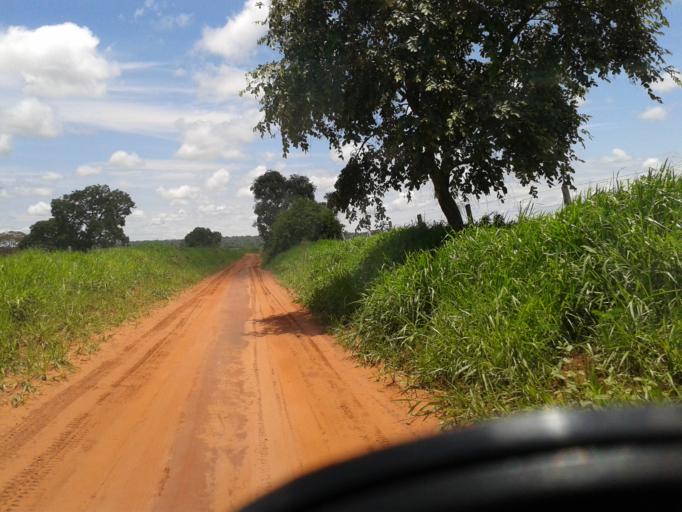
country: BR
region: Minas Gerais
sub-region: Santa Vitoria
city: Santa Vitoria
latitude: -18.9677
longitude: -49.8799
